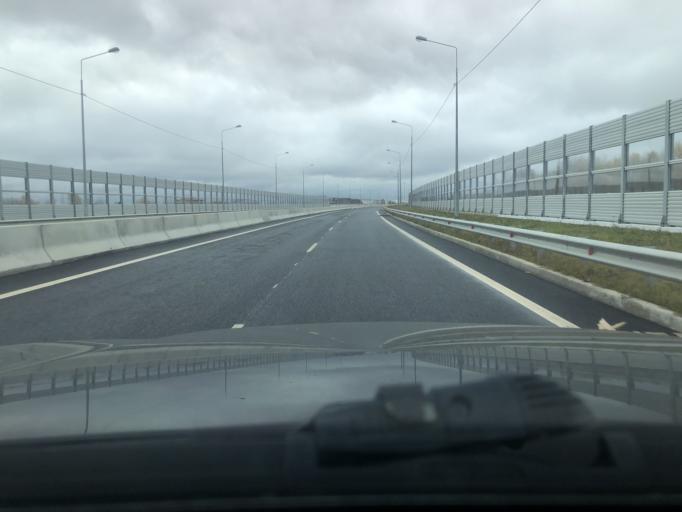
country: RU
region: Moskovskaya
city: Semkhoz
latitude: 56.3158
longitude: 38.0905
